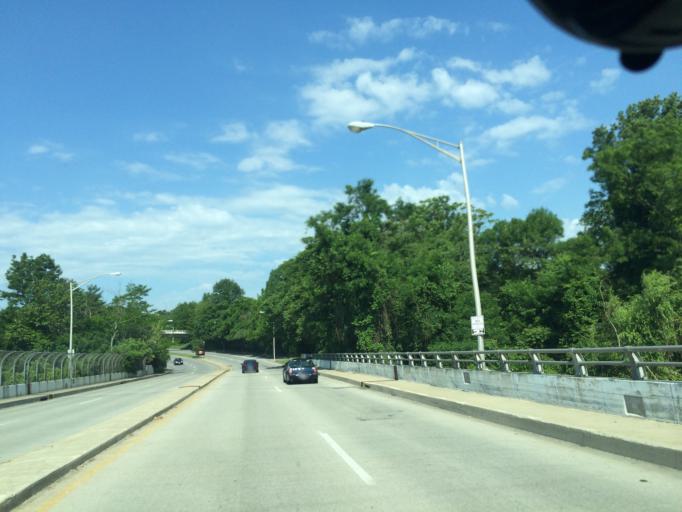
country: US
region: Maryland
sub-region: Baltimore County
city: Parkville
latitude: 39.3686
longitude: -76.5737
